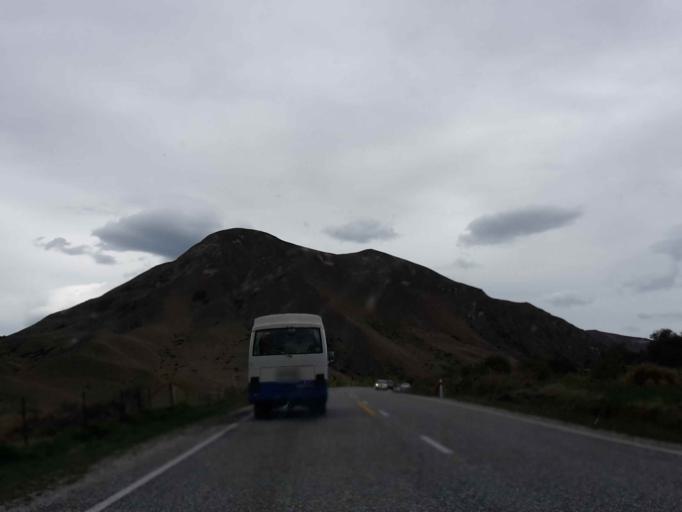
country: NZ
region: Otago
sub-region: Queenstown-Lakes District
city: Wanaka
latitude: -44.5864
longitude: 169.5829
